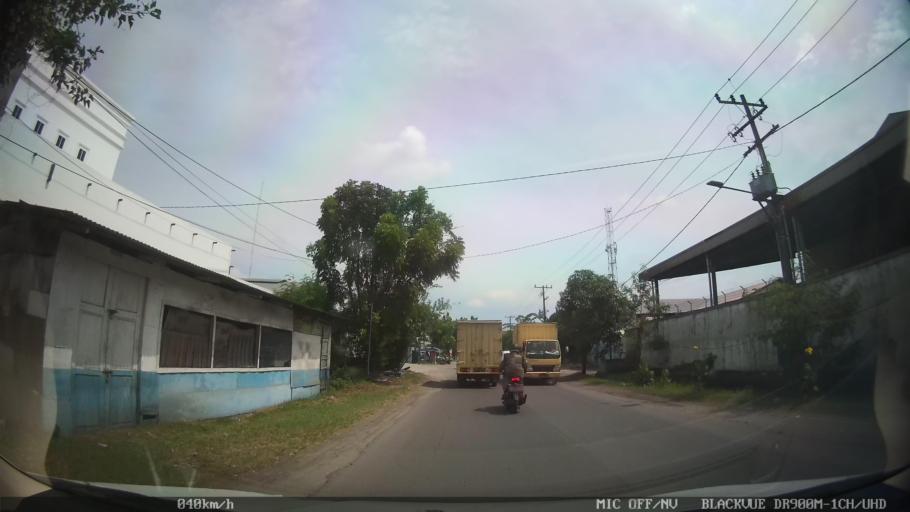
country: ID
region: North Sumatra
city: Medan
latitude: 3.6365
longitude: 98.7163
